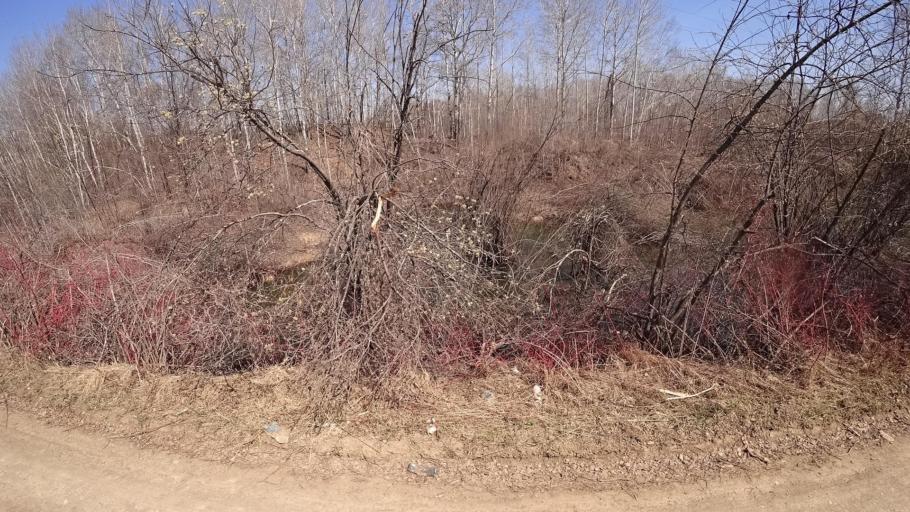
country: RU
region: Khabarovsk Krai
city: Khurba
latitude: 50.4128
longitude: 136.8731
